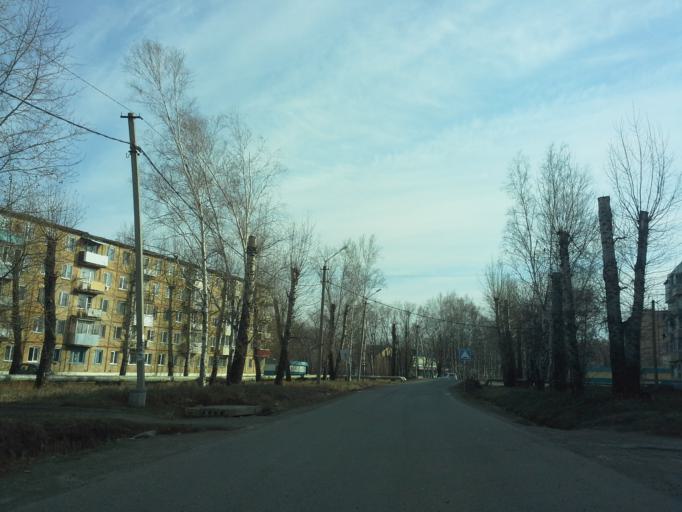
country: RU
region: Khabarovsk Krai
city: Knyaze-Volkonskoye
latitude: 48.4372
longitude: 135.4211
